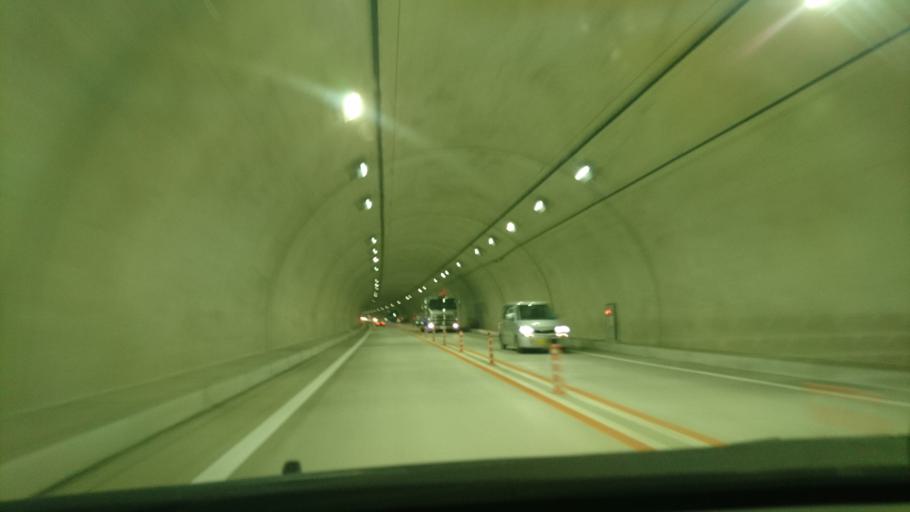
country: JP
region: Iwate
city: Kamaishi
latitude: 39.2683
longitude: 141.8470
